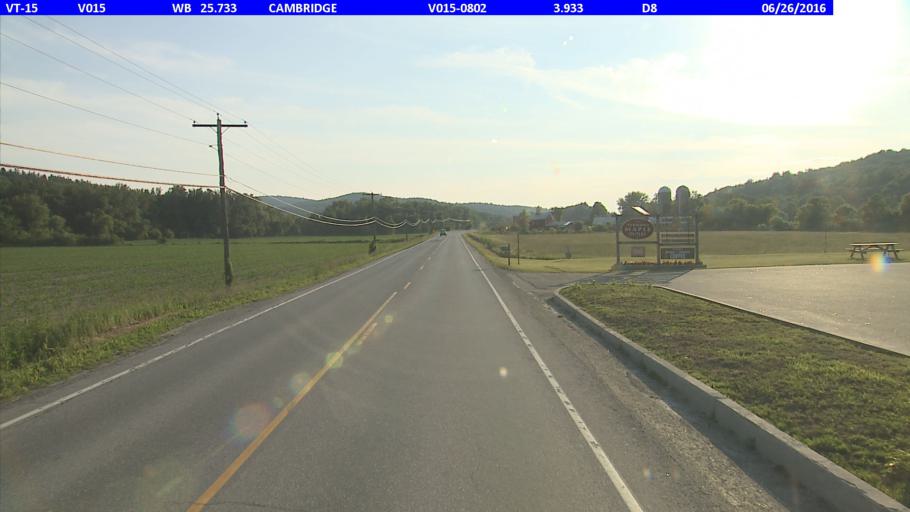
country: US
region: Vermont
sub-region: Lamoille County
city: Johnson
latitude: 44.6454
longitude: -72.8509
